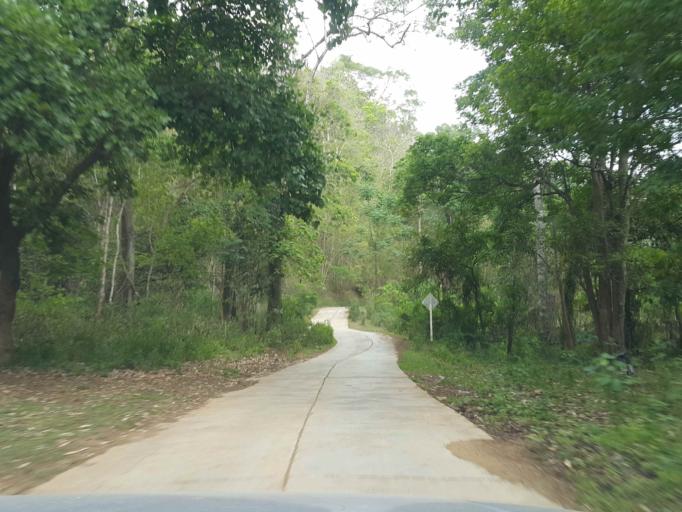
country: TH
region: Chiang Mai
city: Wiang Haeng
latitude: 19.3787
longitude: 98.7488
